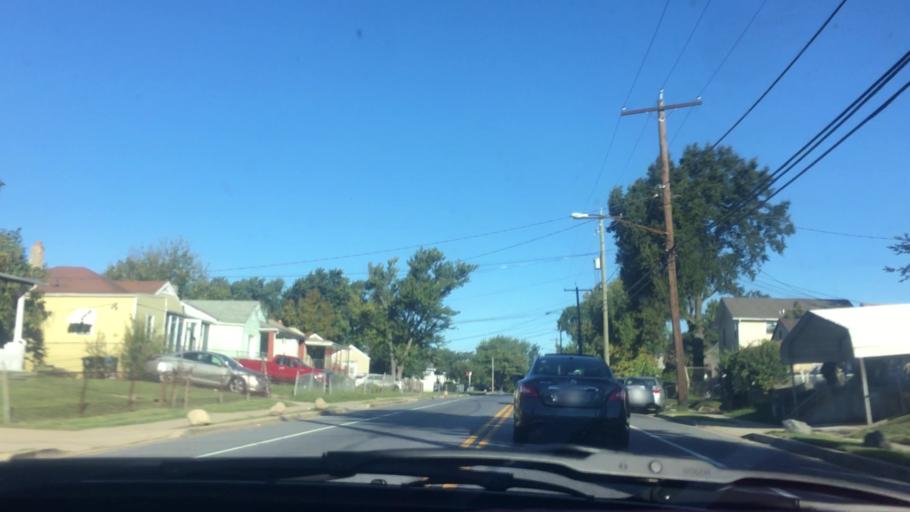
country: US
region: Maryland
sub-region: Prince George's County
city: Fairmount Heights
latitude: 38.9061
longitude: -76.9177
